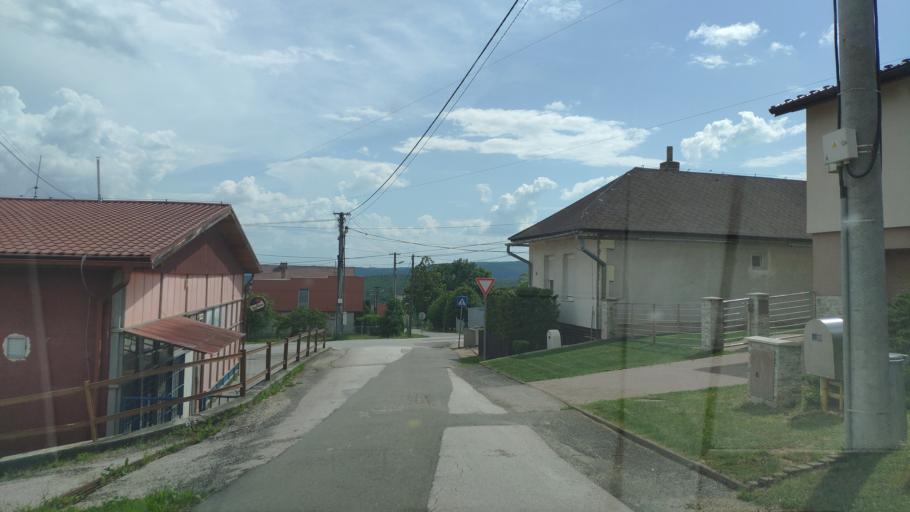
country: SK
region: Kosicky
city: Medzev
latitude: 48.7117
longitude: 20.9733
